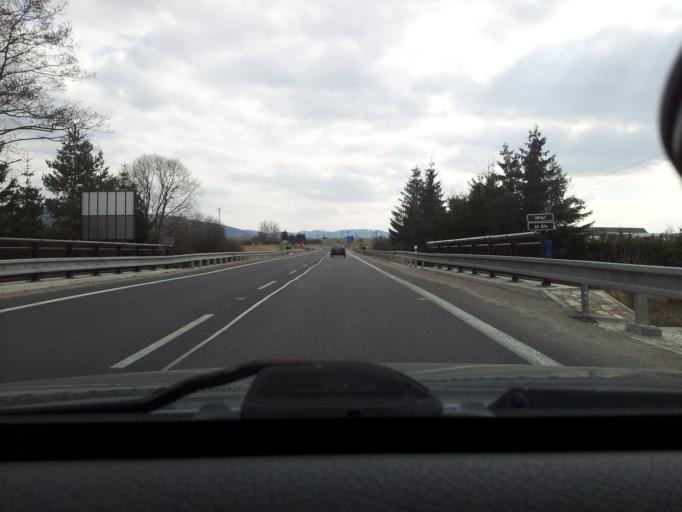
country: SK
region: Banskobystricky
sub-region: Okres Ziar nad Hronom
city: Kremnica
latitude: 48.8458
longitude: 18.8661
